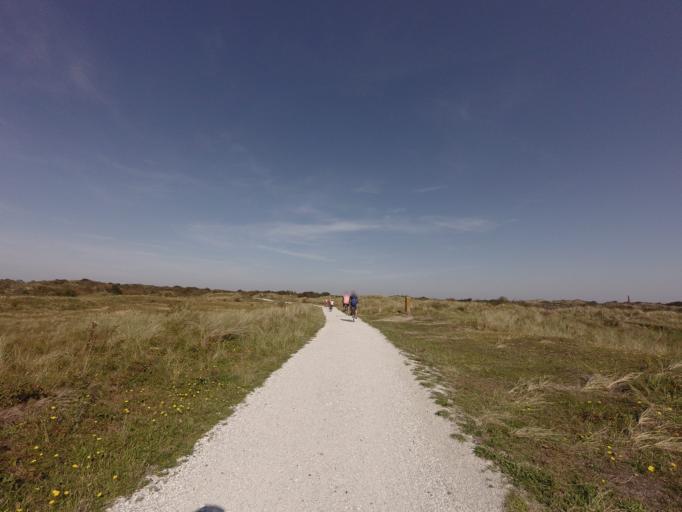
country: NL
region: Friesland
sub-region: Gemeente Schiermonnikoog
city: Schiermonnikoog
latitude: 53.4754
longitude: 6.1400
